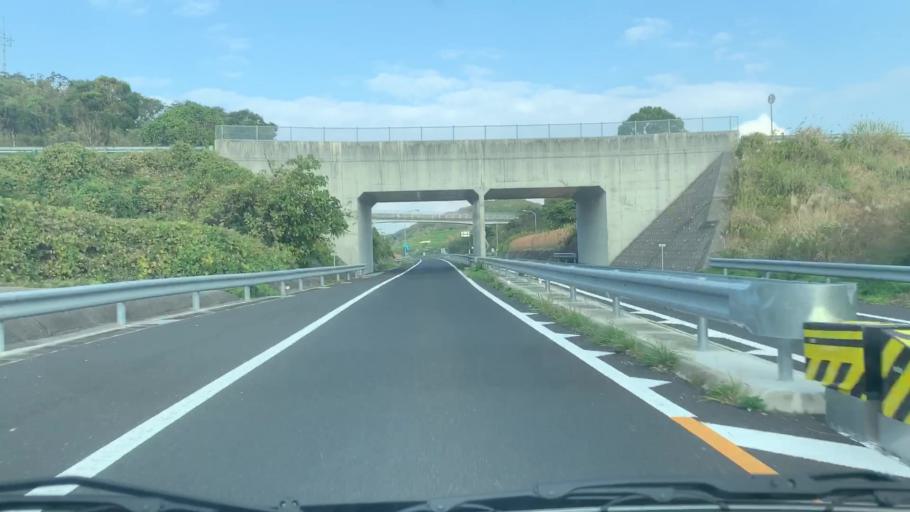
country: JP
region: Nagasaki
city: Sasebo
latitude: 33.0435
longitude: 129.7480
